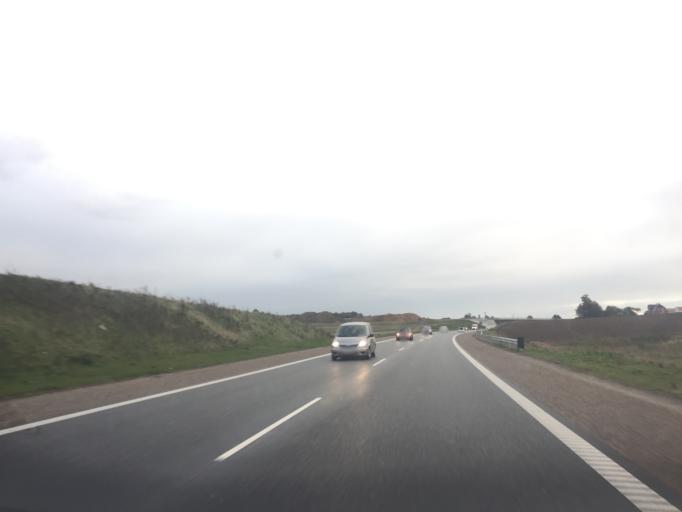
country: DK
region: Capital Region
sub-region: Egedal Kommune
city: Smorumnedre
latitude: 55.7405
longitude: 12.2830
